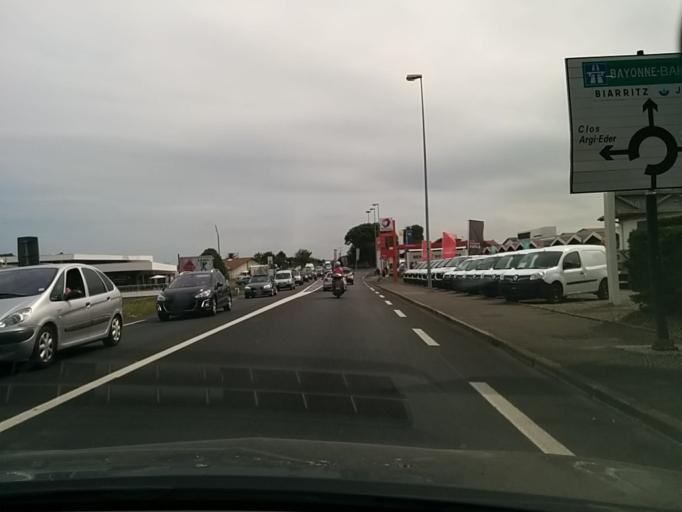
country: FR
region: Aquitaine
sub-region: Departement des Pyrenees-Atlantiques
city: Saint-Jean-de-Luz
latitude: 43.3984
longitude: -1.6425
